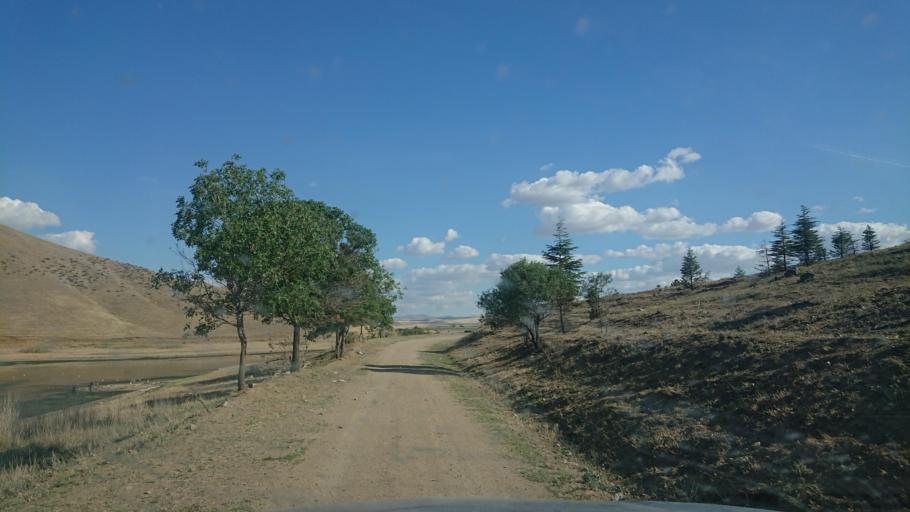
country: TR
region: Aksaray
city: Sariyahsi
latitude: 39.0209
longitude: 33.8964
